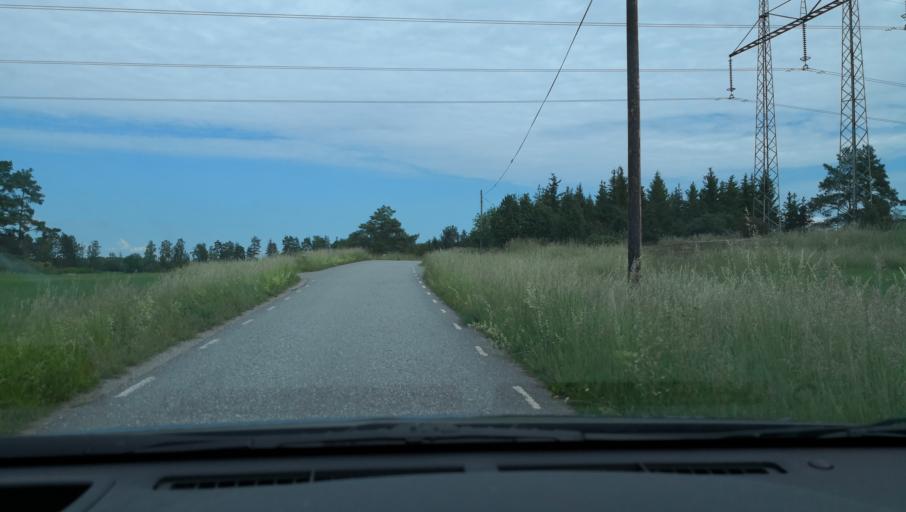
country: SE
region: Uppsala
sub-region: Enkopings Kommun
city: Orsundsbro
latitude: 59.6908
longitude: 17.3849
